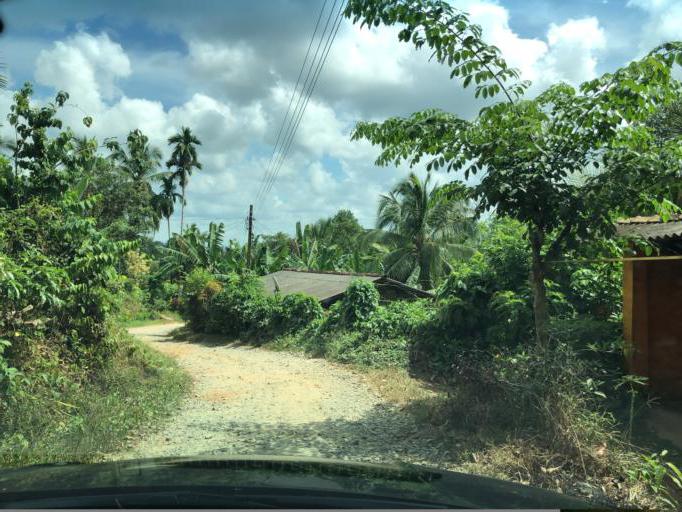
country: LK
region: Western
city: Horawala Junction
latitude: 6.5416
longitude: 80.0956
